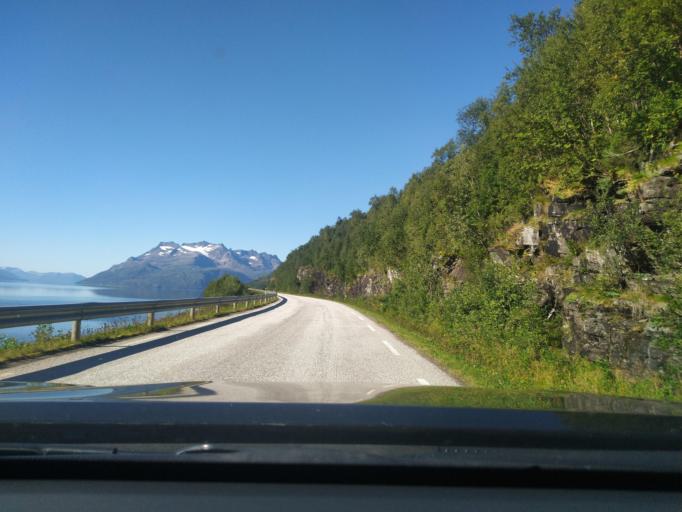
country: NO
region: Troms
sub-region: Dyroy
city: Brostadbotn
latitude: 68.9341
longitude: 17.6955
